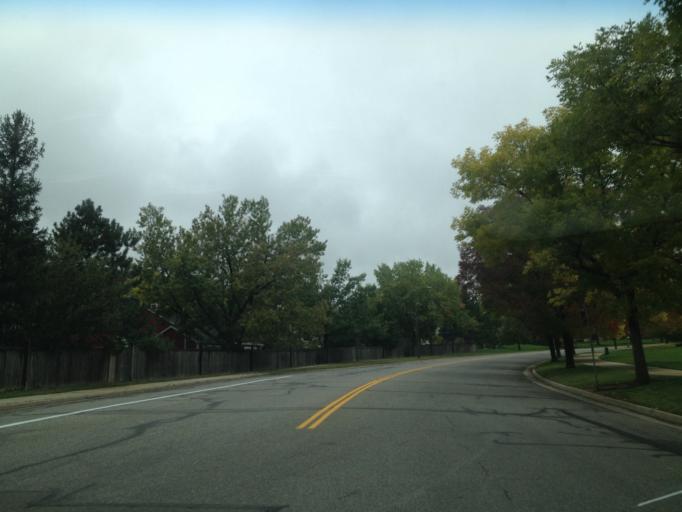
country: US
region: Colorado
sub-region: Boulder County
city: Louisville
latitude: 39.9744
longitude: -105.1511
